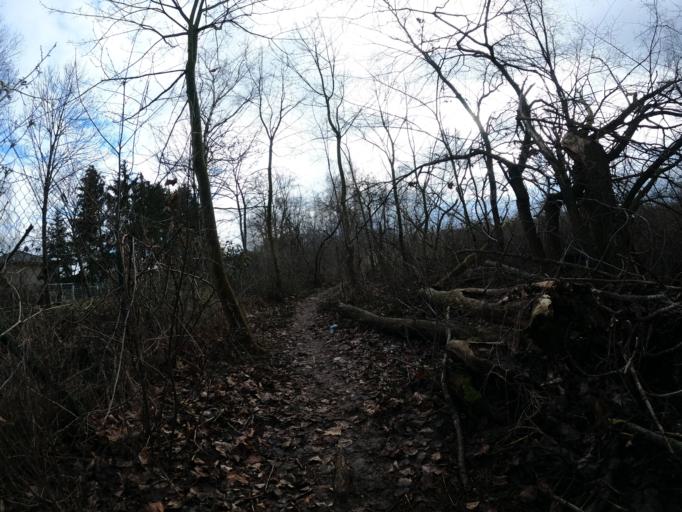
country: DE
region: Berlin
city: Hellersdorf
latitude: 52.5483
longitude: 13.6042
